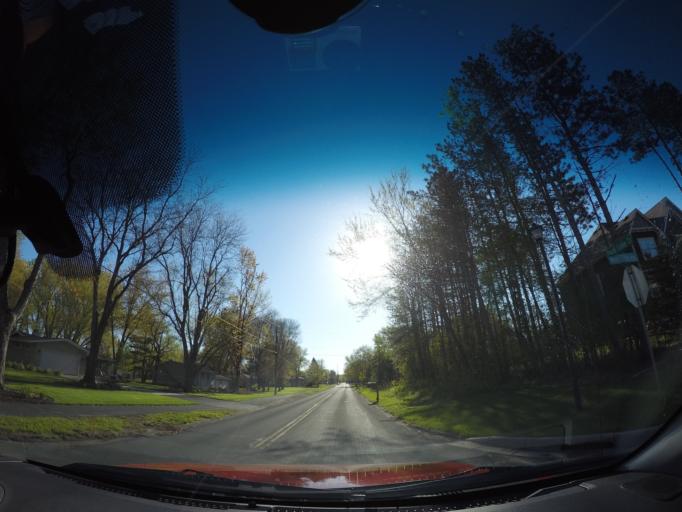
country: US
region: Minnesota
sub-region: Hennepin County
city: Saint Louis Park
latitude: 44.9632
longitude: -93.3712
